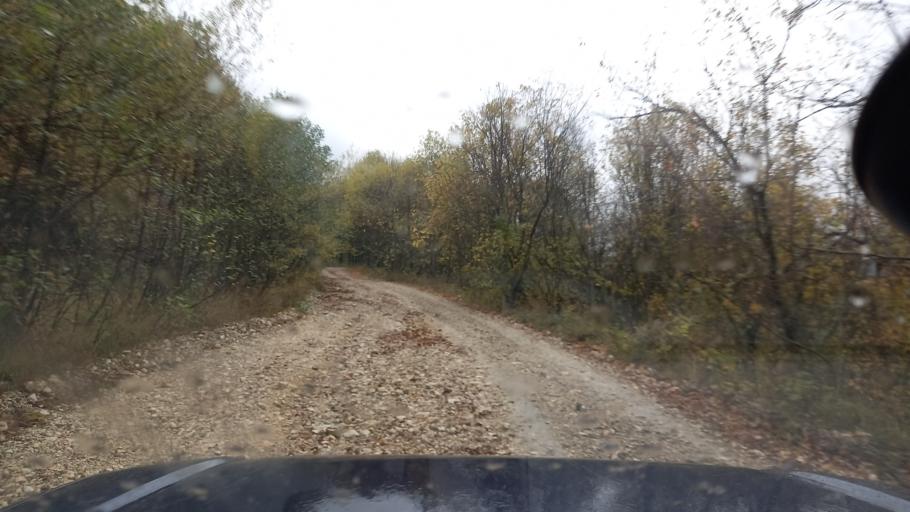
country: RU
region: Krasnodarskiy
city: Neftegorsk
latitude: 44.0230
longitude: 39.8385
